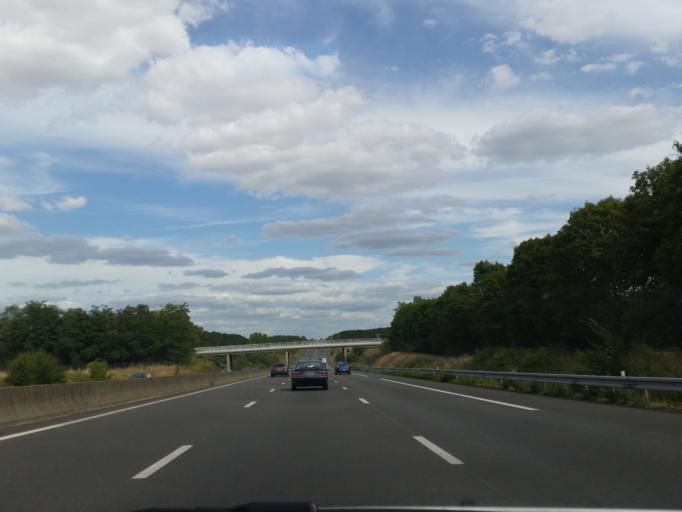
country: FR
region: Centre
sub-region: Departement du Loir-et-Cher
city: Saint-Sulpice-de-Pommeray
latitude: 47.6193
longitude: 1.2460
